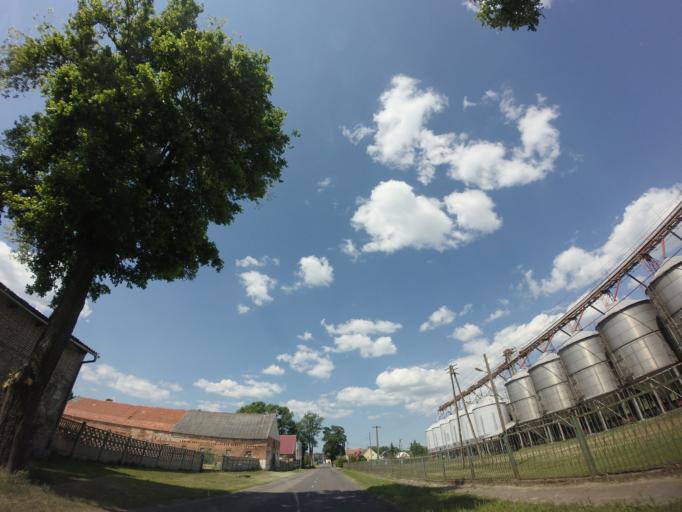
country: PL
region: West Pomeranian Voivodeship
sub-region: Powiat choszczenski
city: Pelczyce
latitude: 53.1154
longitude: 15.2527
